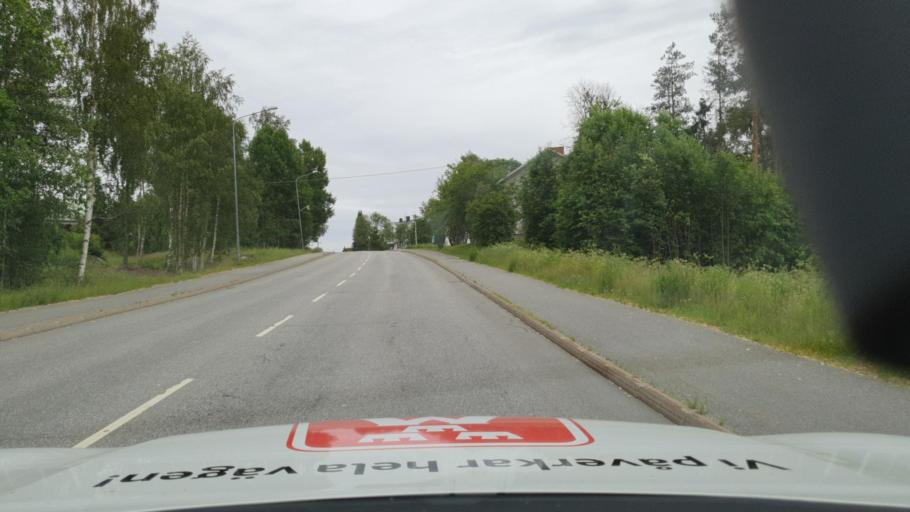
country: SE
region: Vaesterbotten
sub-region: Nordmalings Kommun
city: Nordmaling
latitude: 63.5428
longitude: 19.4391
